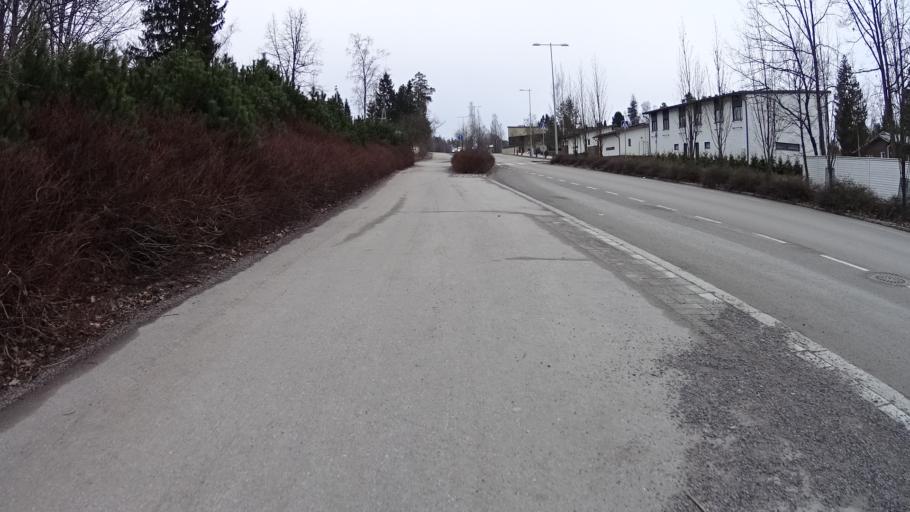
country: FI
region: Uusimaa
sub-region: Helsinki
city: Kauniainen
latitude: 60.2367
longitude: 24.7434
